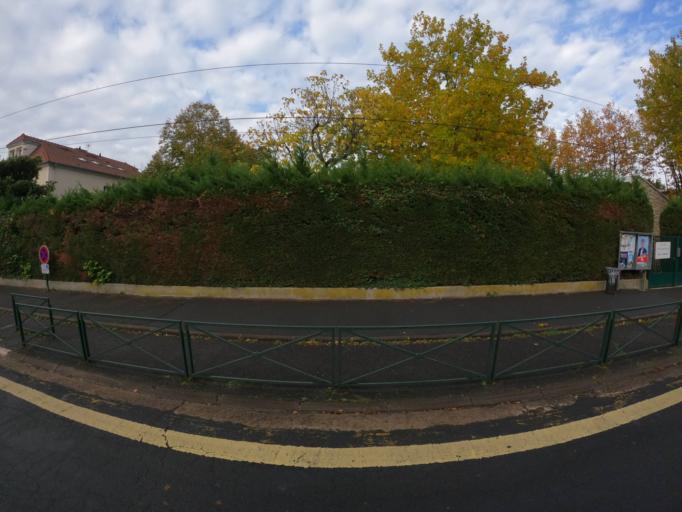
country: FR
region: Ile-de-France
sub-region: Departement de Seine-Saint-Denis
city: Montfermeil
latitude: 48.9005
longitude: 2.5942
